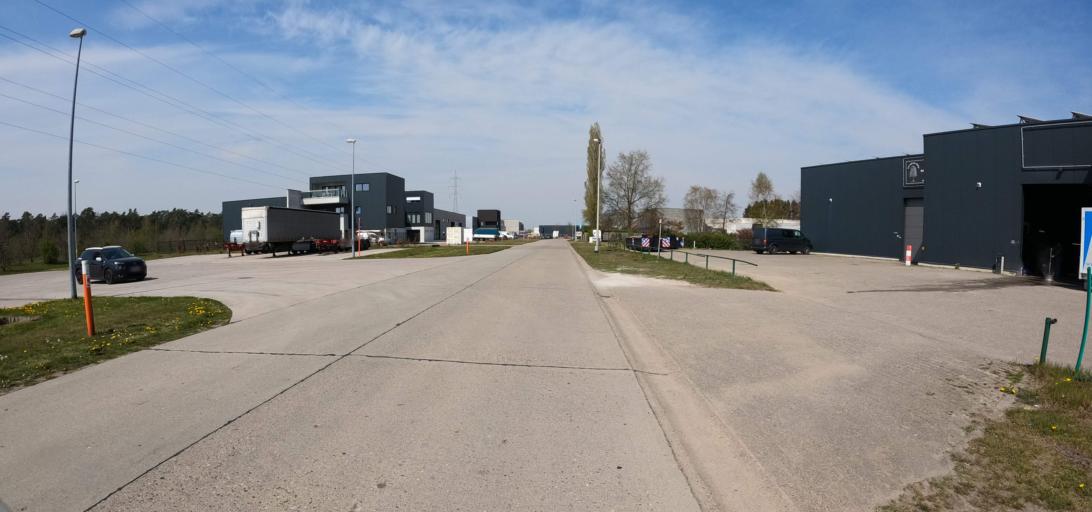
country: BE
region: Flanders
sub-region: Provincie Antwerpen
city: Beerse
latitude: 51.2983
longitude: 4.8308
